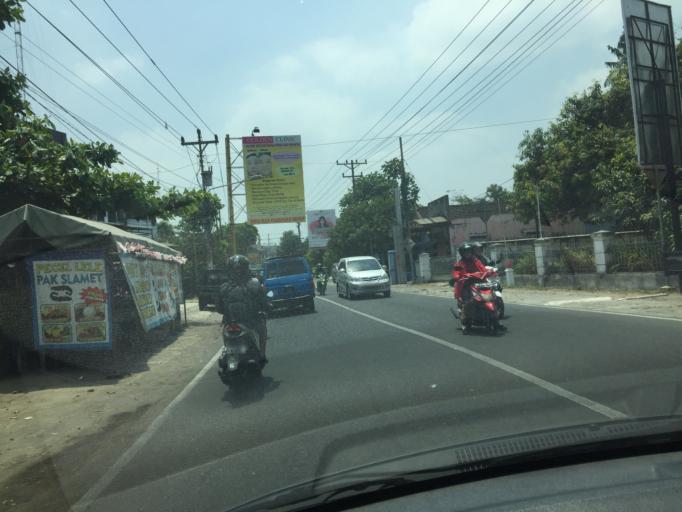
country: ID
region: Daerah Istimewa Yogyakarta
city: Melati
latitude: -7.7498
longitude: 110.3719
